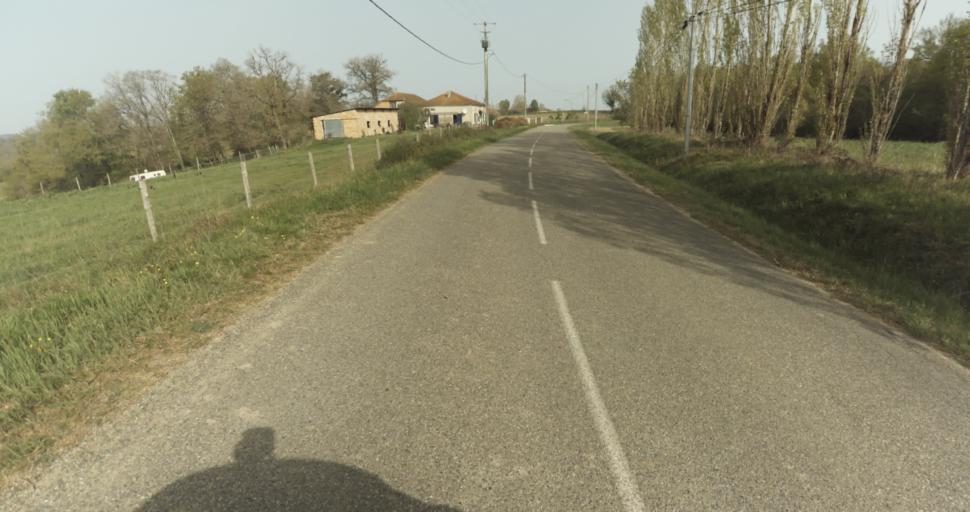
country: FR
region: Midi-Pyrenees
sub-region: Departement du Tarn-et-Garonne
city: Moissac
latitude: 44.1551
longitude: 1.0638
